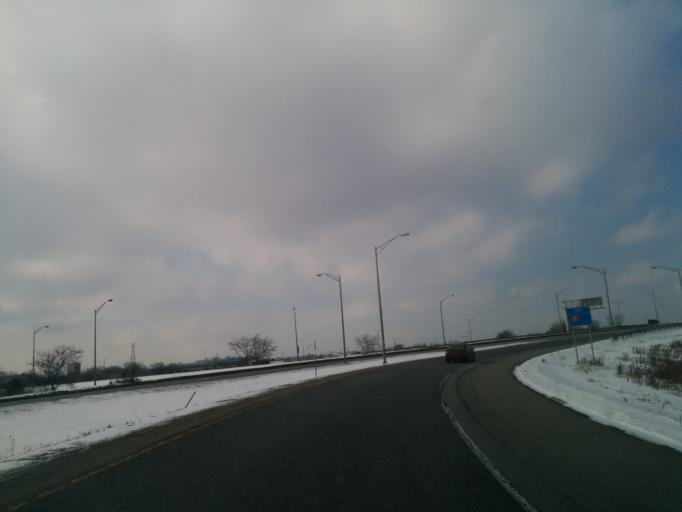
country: US
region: Illinois
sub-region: Cook County
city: Tinley Park
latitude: 41.5493
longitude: -87.7916
